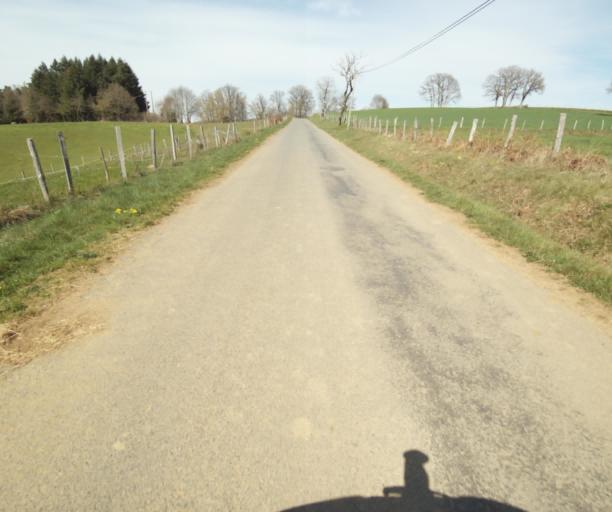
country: FR
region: Limousin
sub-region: Departement de la Correze
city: Seilhac
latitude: 45.3948
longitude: 1.7840
